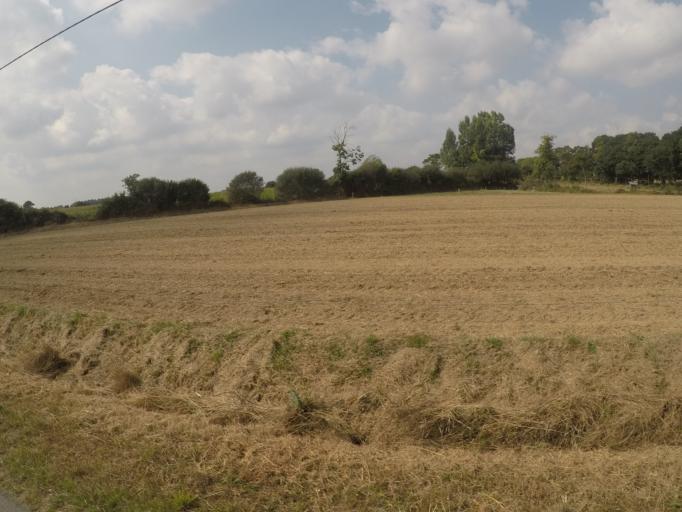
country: FR
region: Brittany
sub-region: Departement des Cotes-d'Armor
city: Saint-Donan
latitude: 48.5124
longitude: -2.9127
